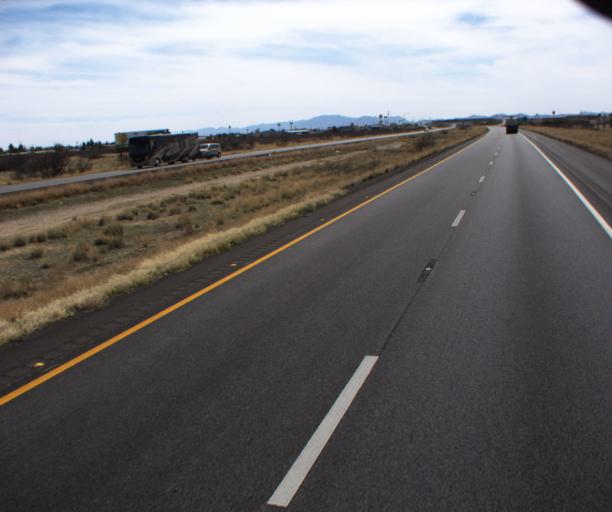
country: US
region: Arizona
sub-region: Cochise County
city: Willcox
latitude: 32.2741
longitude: -109.8378
